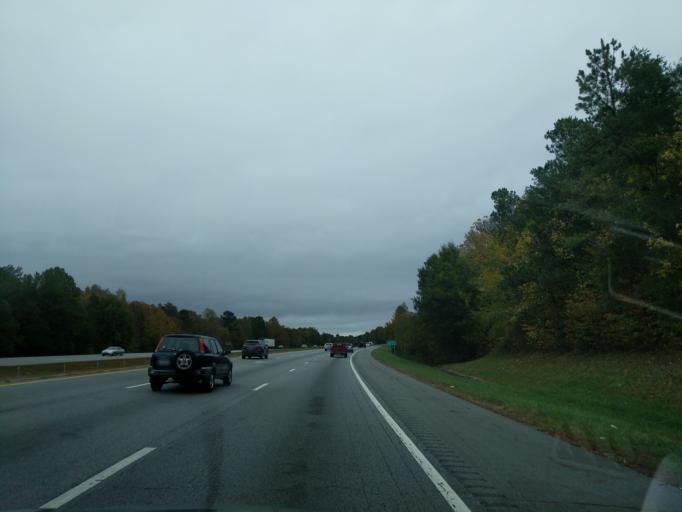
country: US
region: North Carolina
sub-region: Randolph County
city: Archdale
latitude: 35.8960
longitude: -79.9717
